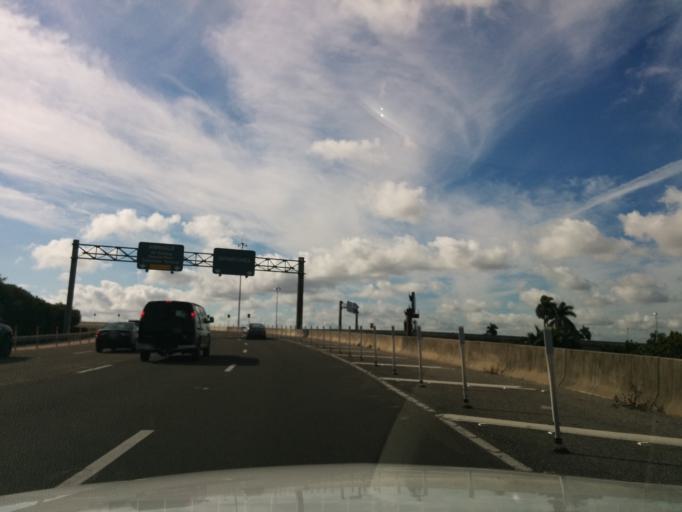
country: US
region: Florida
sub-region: Broward County
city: Dania Beach
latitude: 26.0709
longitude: -80.1355
